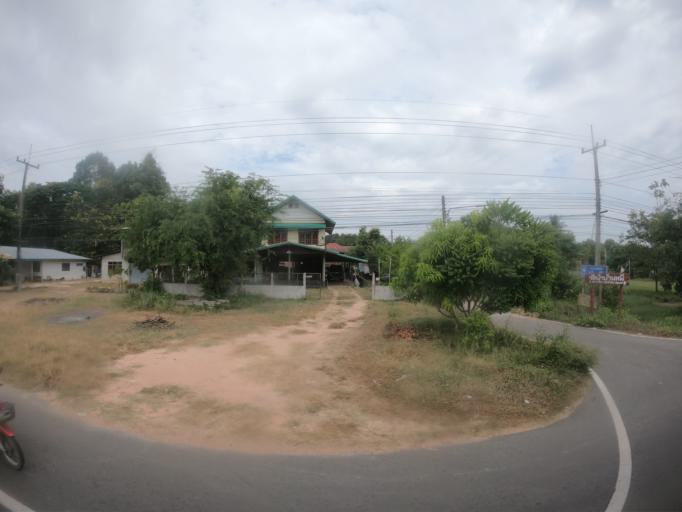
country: TH
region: Kalasin
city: Khong Chai
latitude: 16.1391
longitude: 103.4352
